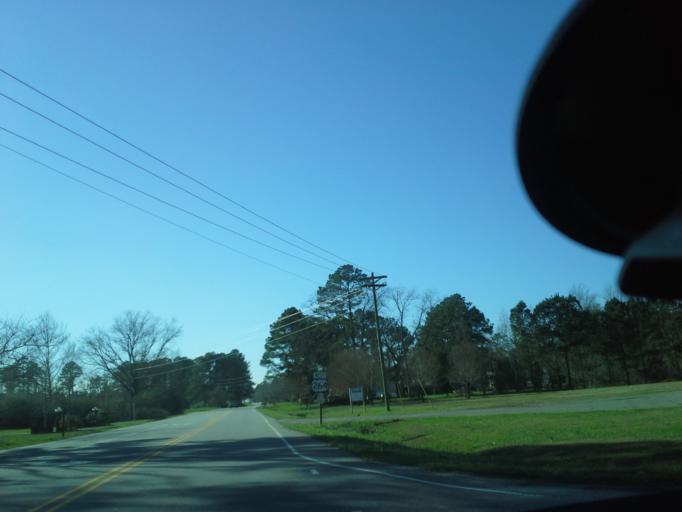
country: US
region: North Carolina
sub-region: Beaufort County
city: Belhaven
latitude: 35.5337
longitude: -76.7265
